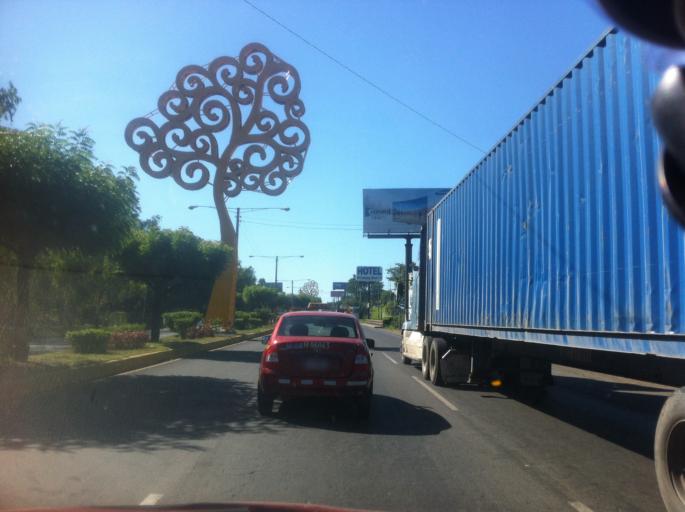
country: NI
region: Managua
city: Managua
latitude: 12.1468
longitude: -86.1829
